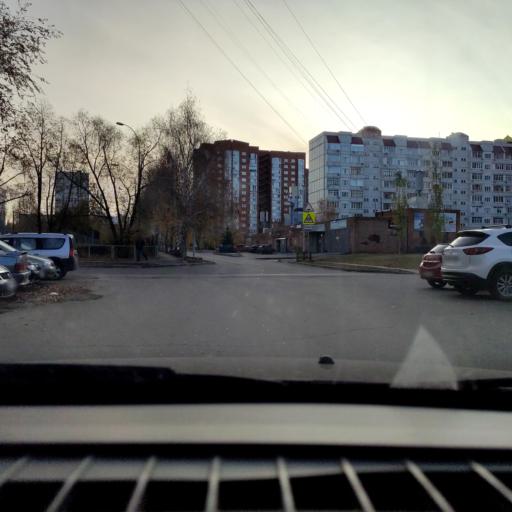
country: RU
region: Samara
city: Tol'yatti
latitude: 53.5020
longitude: 49.2817
